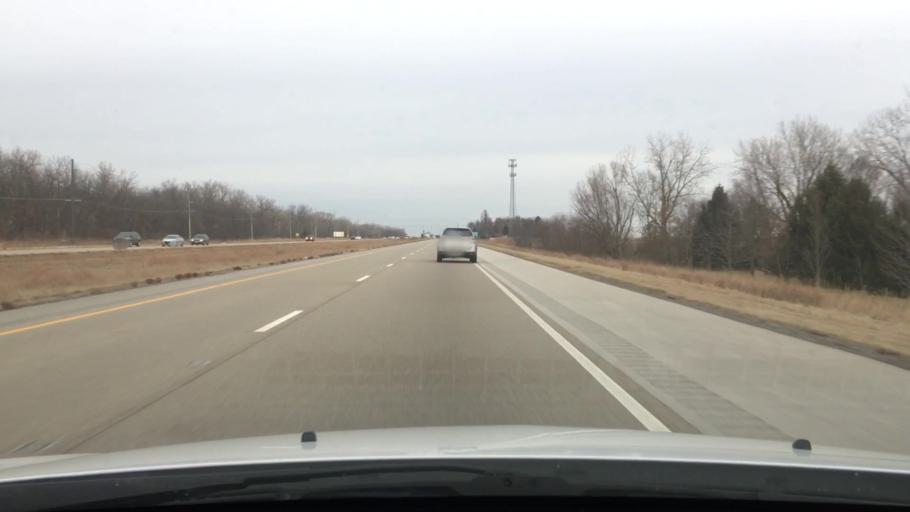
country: US
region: Illinois
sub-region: Logan County
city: Atlanta
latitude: 40.2417
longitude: -89.2562
